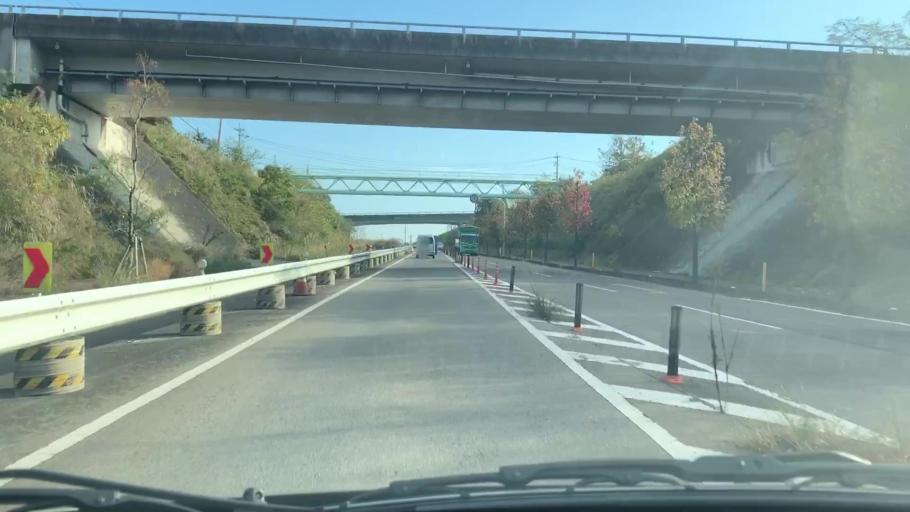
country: JP
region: Saga Prefecture
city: Kashima
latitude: 33.1021
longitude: 130.0867
